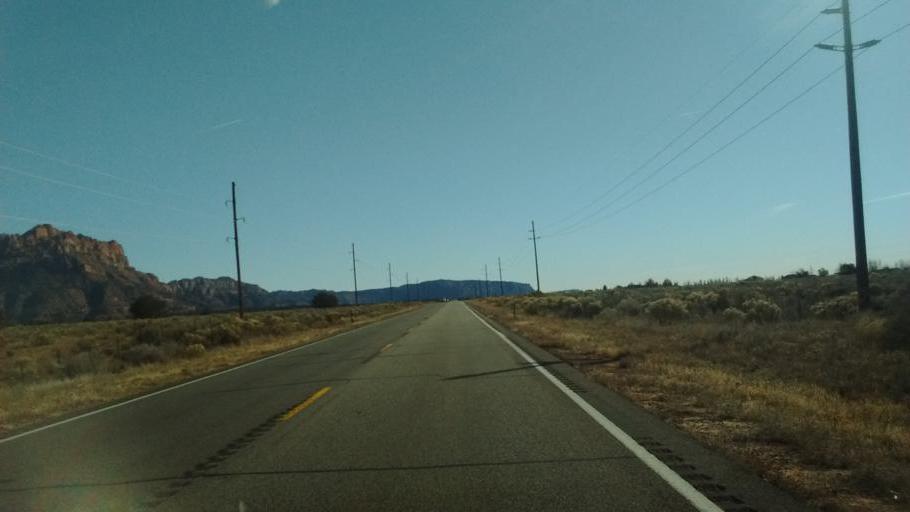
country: US
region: Arizona
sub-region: Mohave County
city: Colorado City
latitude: 37.0314
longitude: -113.0580
